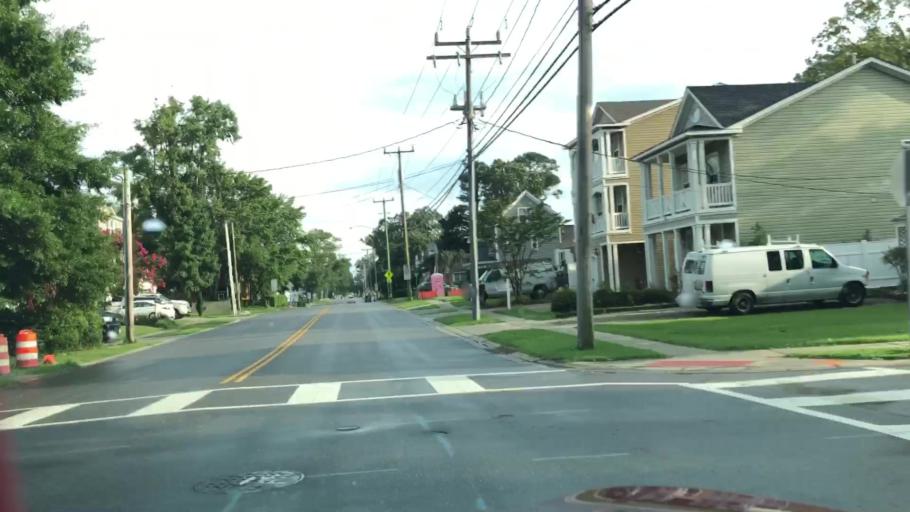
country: US
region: Virginia
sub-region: City of Virginia Beach
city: Virginia Beach
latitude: 36.8405
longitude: -75.9801
